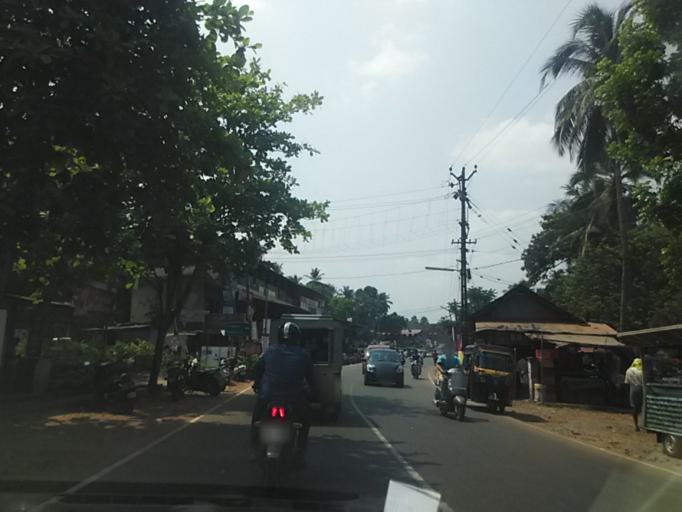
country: IN
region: Kerala
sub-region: Kozhikode
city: Naduvannur
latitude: 11.4891
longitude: 75.7749
